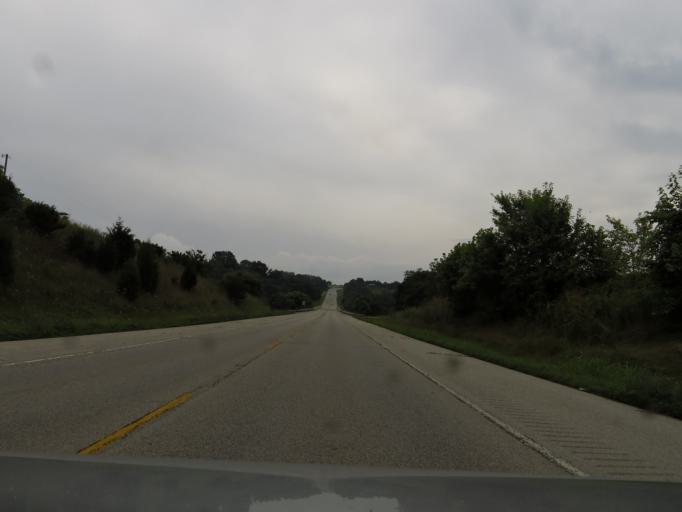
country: US
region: Ohio
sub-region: Brown County
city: Aberdeen
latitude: 38.5718
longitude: -83.8266
